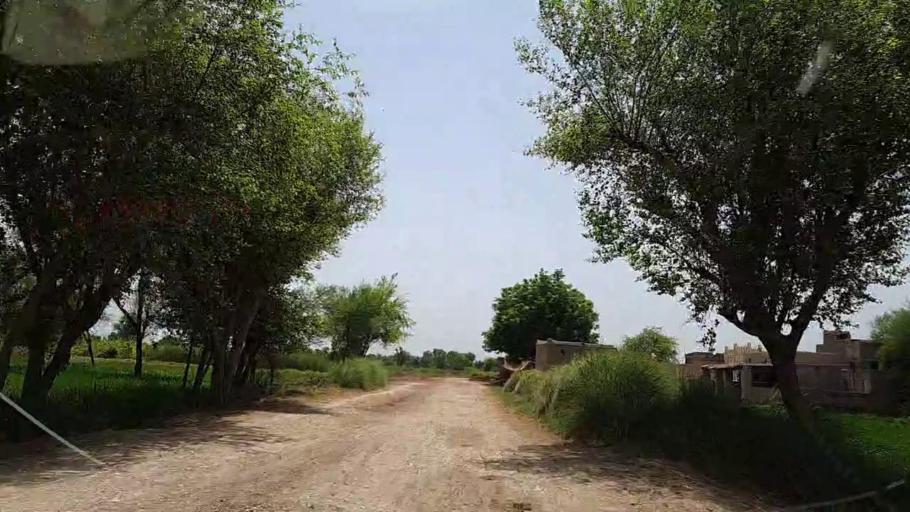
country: PK
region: Sindh
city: Tharu Shah
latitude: 26.9247
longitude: 68.0416
